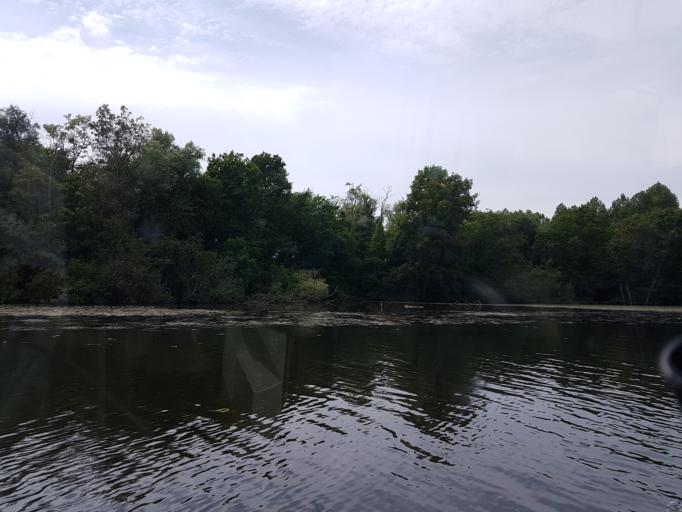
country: FR
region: Bourgogne
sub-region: Departement de l'Yonne
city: Gurgy
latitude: 47.8622
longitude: 3.5521
